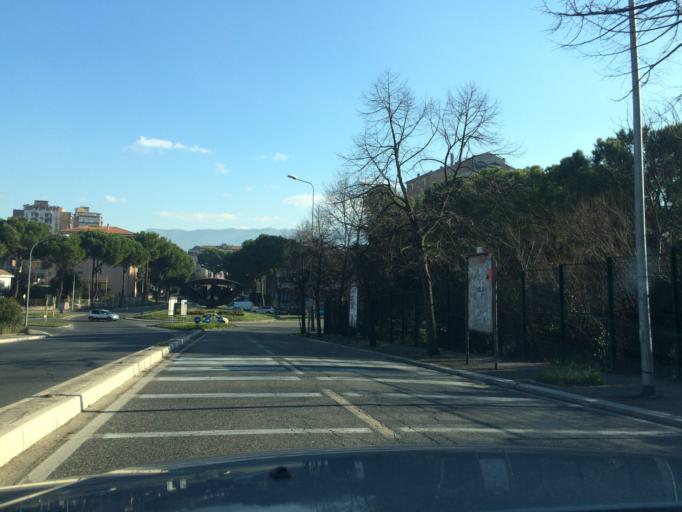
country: IT
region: Umbria
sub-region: Provincia di Terni
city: Terni
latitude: 42.5654
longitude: 12.6369
